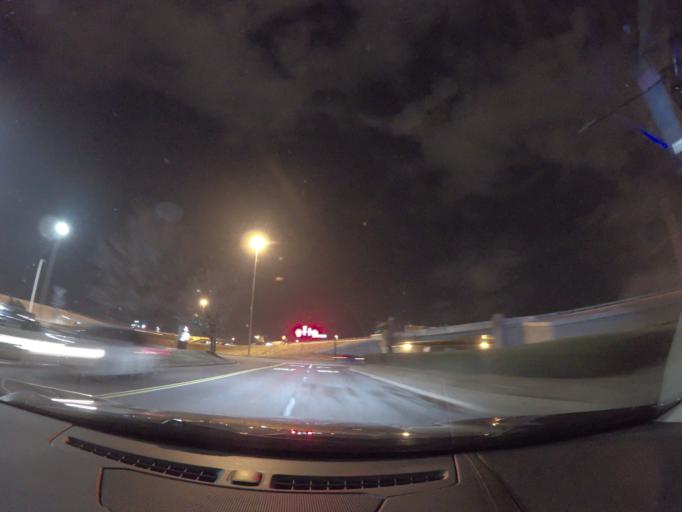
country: US
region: Indiana
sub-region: Clark County
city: Jeffersonville
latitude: 38.2715
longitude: -85.7480
